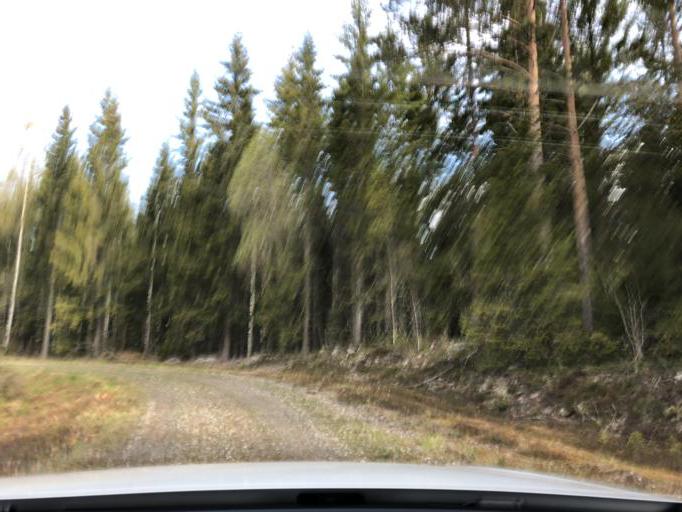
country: SE
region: Uppsala
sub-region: Heby Kommun
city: Tarnsjo
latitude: 60.2944
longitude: 16.8235
